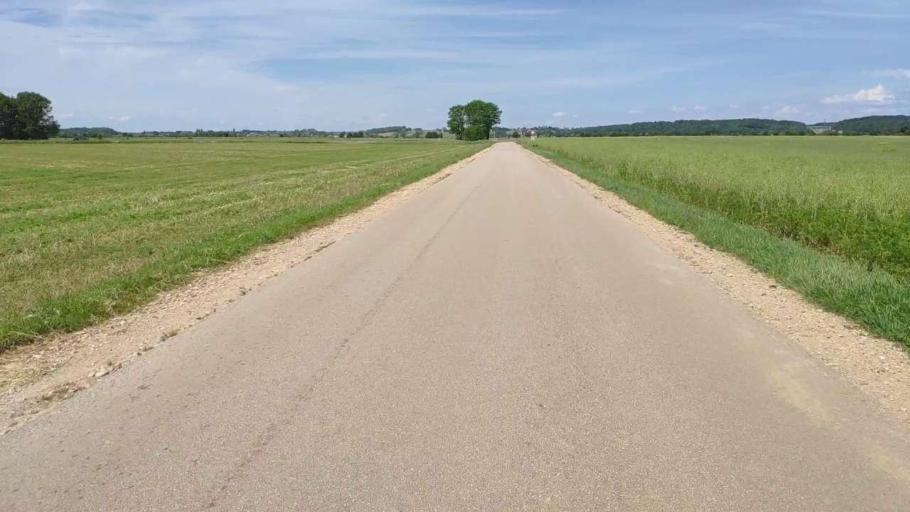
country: FR
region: Franche-Comte
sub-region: Departement du Jura
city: Bletterans
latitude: 46.7536
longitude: 5.4956
